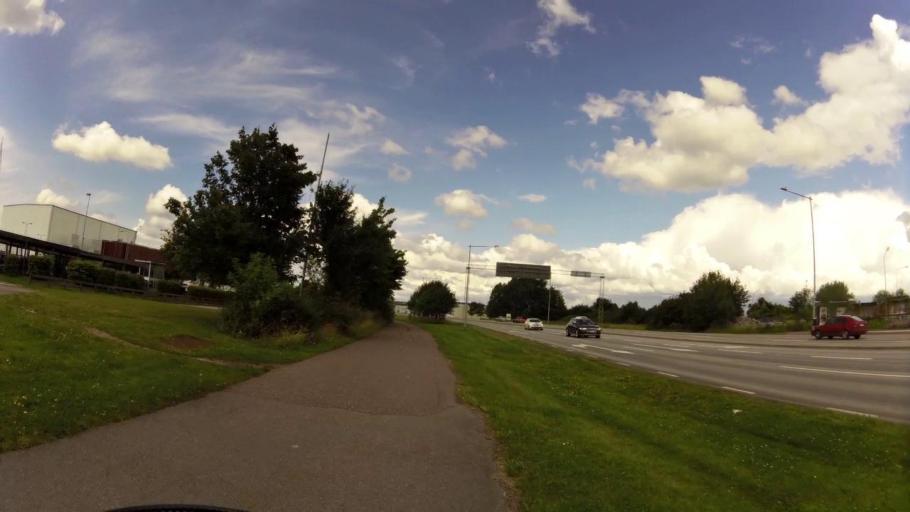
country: SE
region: OEstergoetland
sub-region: Linkopings Kommun
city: Linkoping
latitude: 58.4247
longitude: 15.6150
